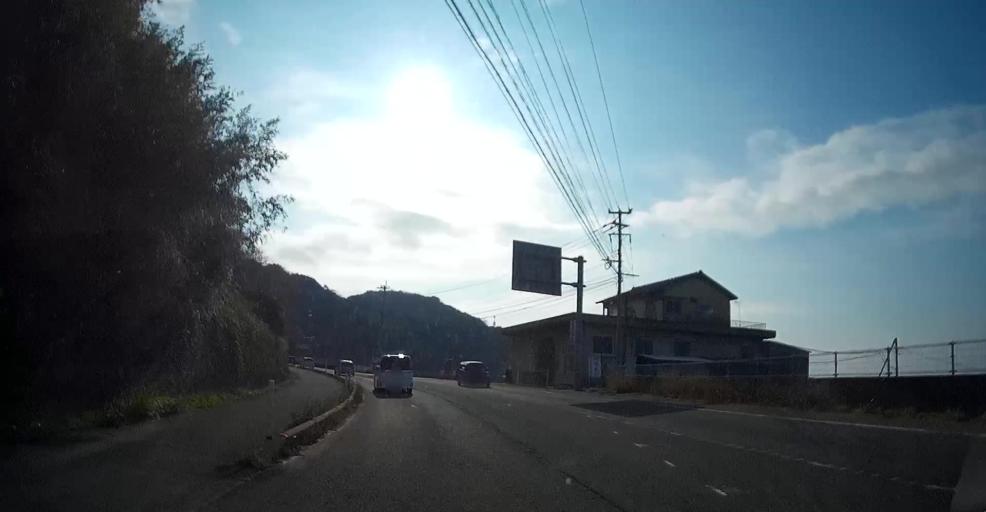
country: JP
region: Kumamoto
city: Yatsushiro
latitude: 32.5701
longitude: 130.4155
